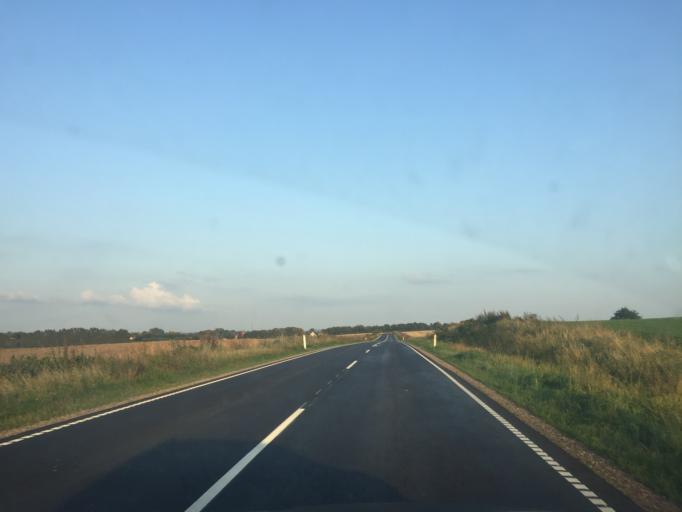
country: DK
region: Zealand
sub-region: Holbaek Kommune
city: Tollose
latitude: 55.5428
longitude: 11.6945
